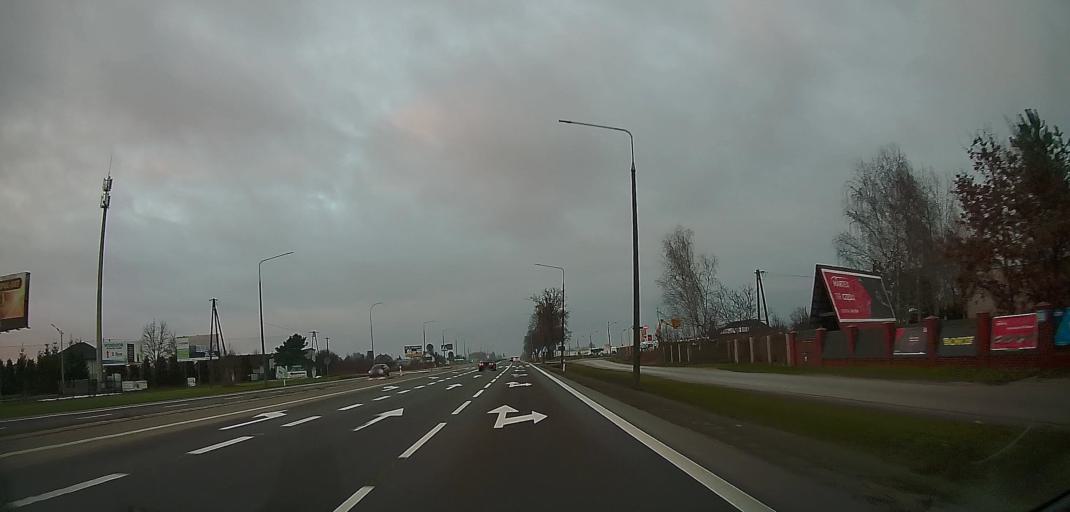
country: PL
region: Masovian Voivodeship
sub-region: Powiat radomski
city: Jedlinsk
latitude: 51.4711
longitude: 21.1353
